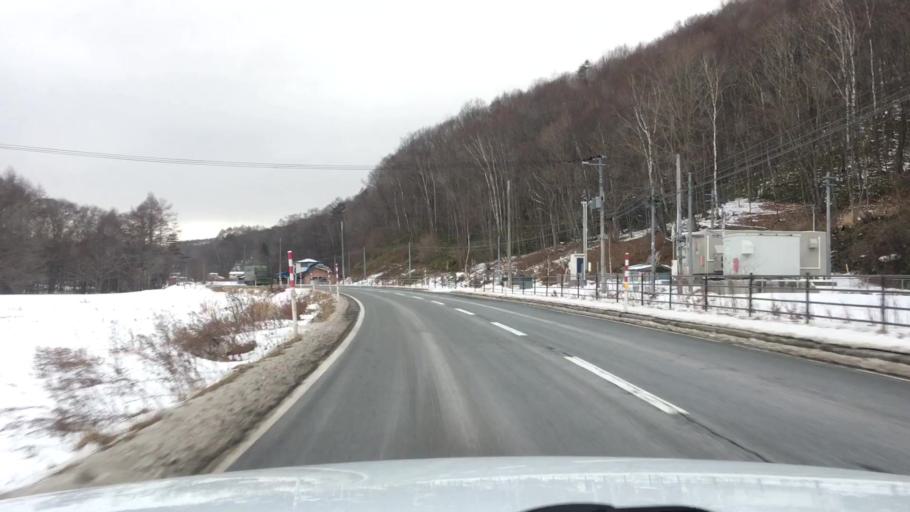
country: JP
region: Iwate
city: Morioka-shi
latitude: 39.6411
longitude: 141.4217
